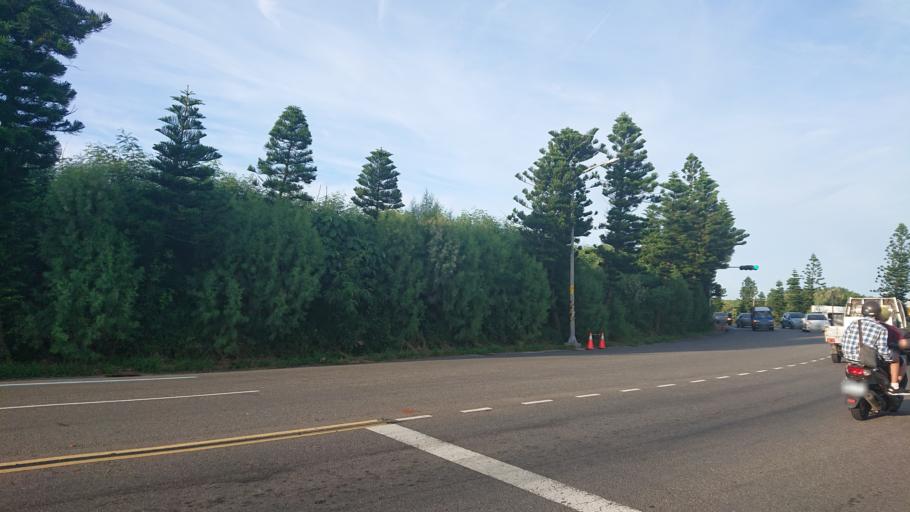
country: TW
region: Taiwan
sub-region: Penghu
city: Ma-kung
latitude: 23.6596
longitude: 119.5631
